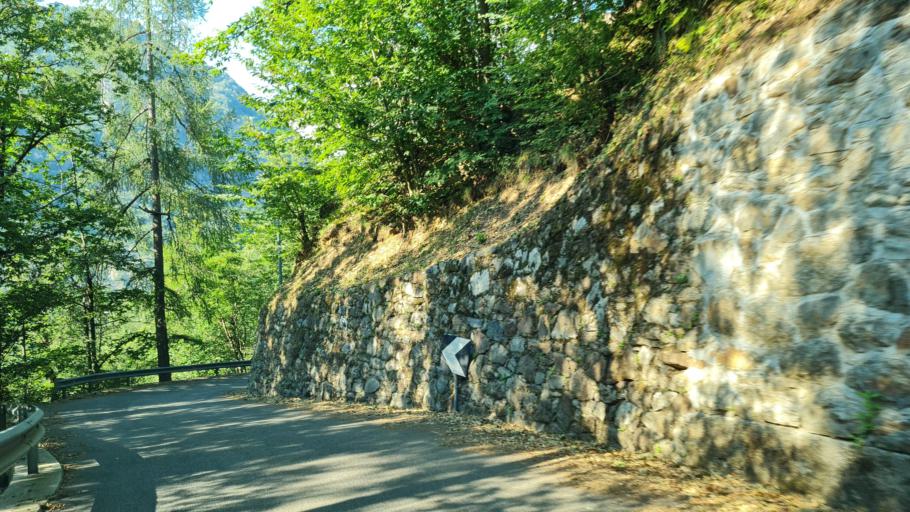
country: IT
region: Aosta Valley
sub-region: Valle d'Aosta
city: Lillianes
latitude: 45.6310
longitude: 7.8485
